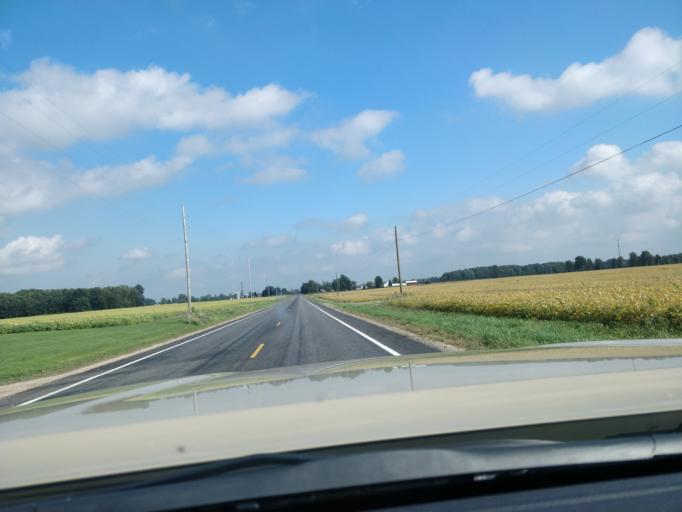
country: US
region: Michigan
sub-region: Ionia County
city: Lake Odessa
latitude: 42.8861
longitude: -85.1141
